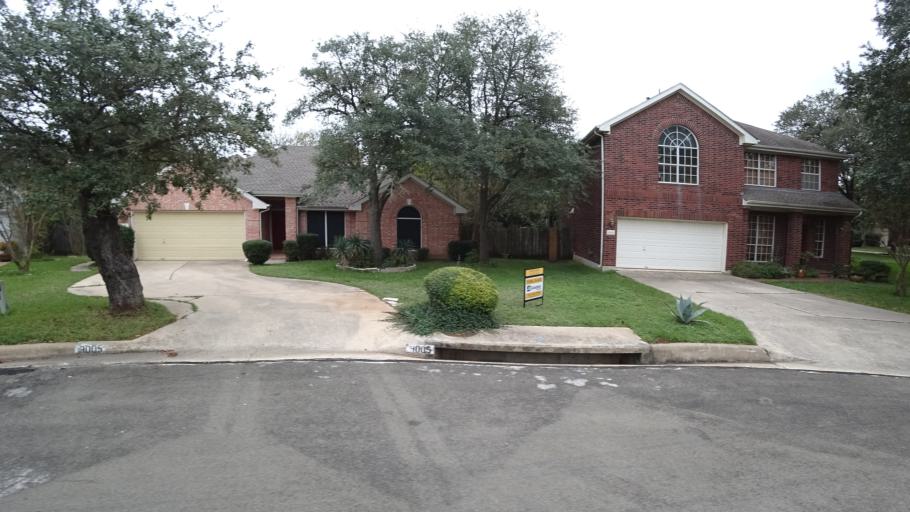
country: US
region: Texas
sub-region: Travis County
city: Shady Hollow
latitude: 30.2114
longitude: -97.8835
